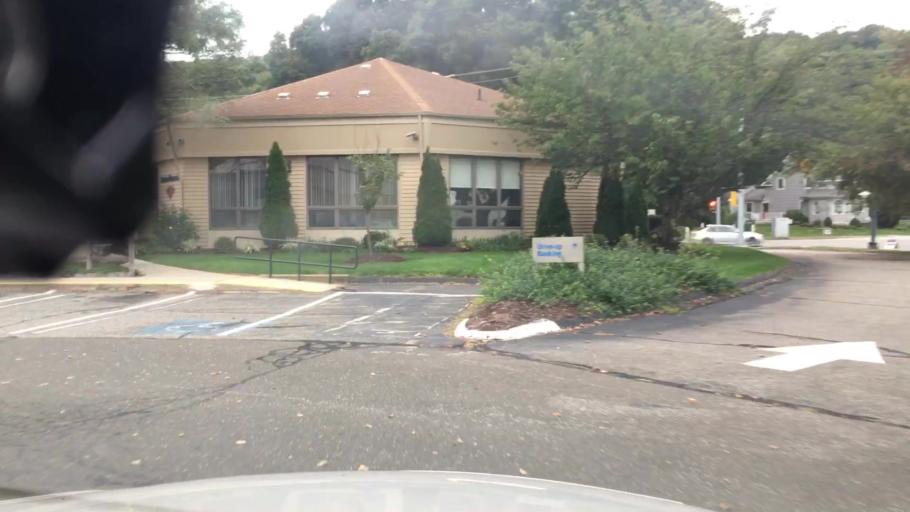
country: US
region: Connecticut
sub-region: Middlesex County
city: Essex Village
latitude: 41.3401
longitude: -72.4138
